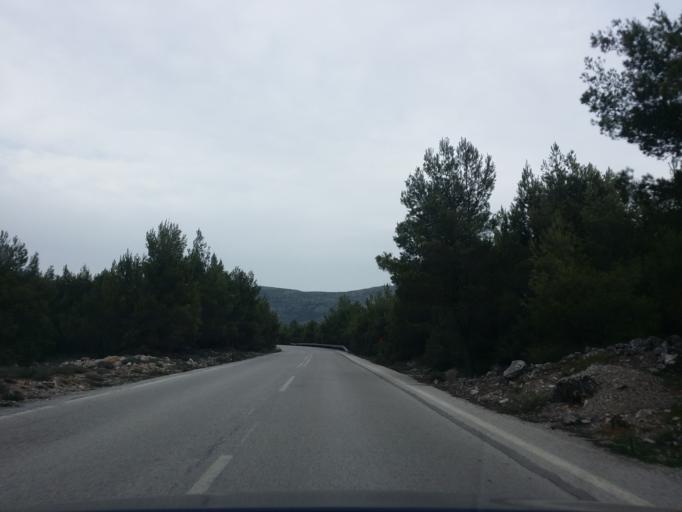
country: GR
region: Attica
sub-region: Nomarchia Dytikis Attikis
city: Vilia
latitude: 38.1523
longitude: 23.2987
